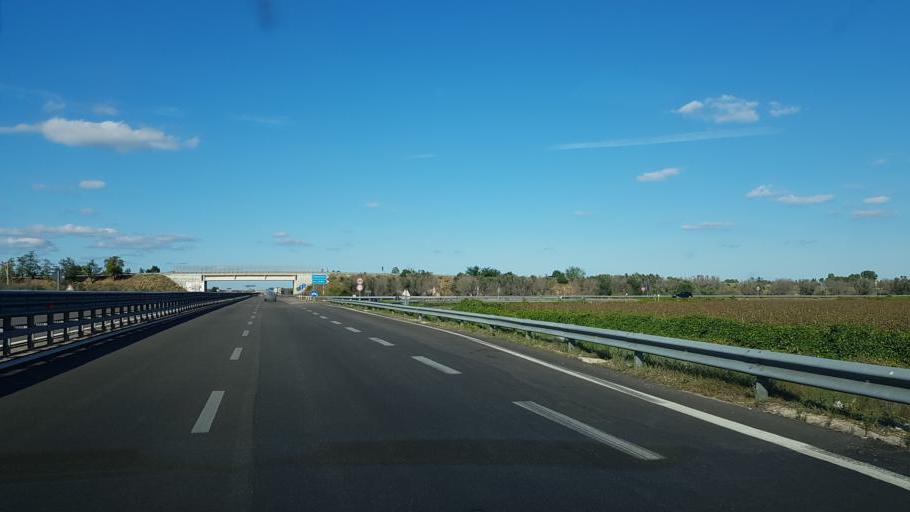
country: IT
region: Apulia
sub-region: Provincia di Lecce
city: Collemeto
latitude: 40.2556
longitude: 18.1179
